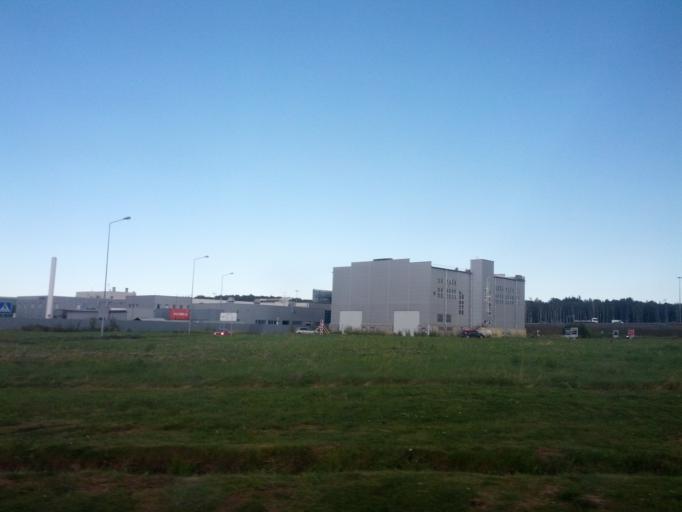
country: RU
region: Leningrad
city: Rybatskoye
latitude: 59.8964
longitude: 30.5187
